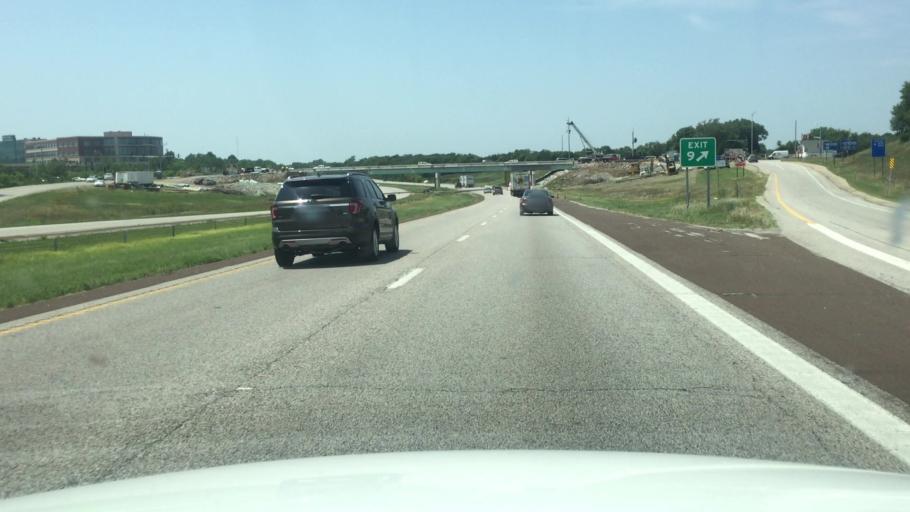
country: US
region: Missouri
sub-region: Jackson County
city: Lees Summit
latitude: 38.9449
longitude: -94.3751
